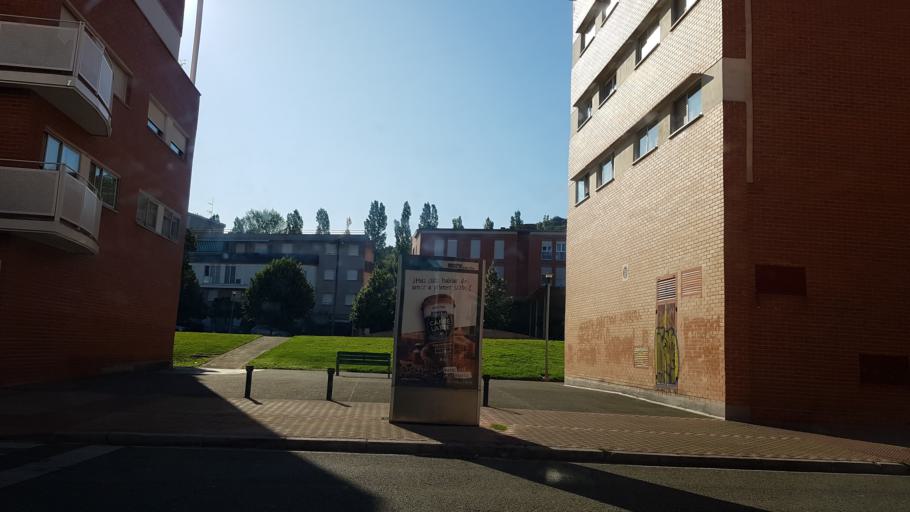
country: ES
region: Navarre
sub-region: Provincia de Navarra
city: Burlata
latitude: 42.8114
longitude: -1.6109
